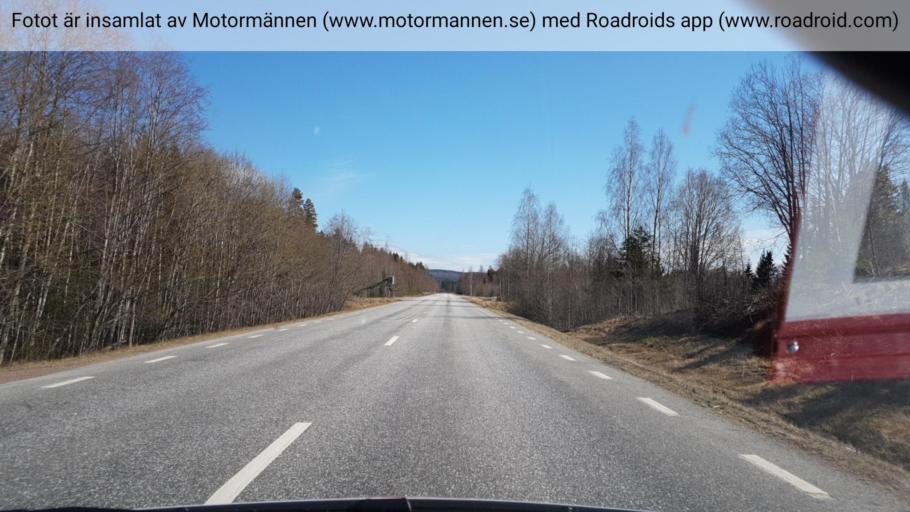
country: SE
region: Vaesternorrland
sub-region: Solleftea Kommun
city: As
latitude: 63.5806
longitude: 16.8254
